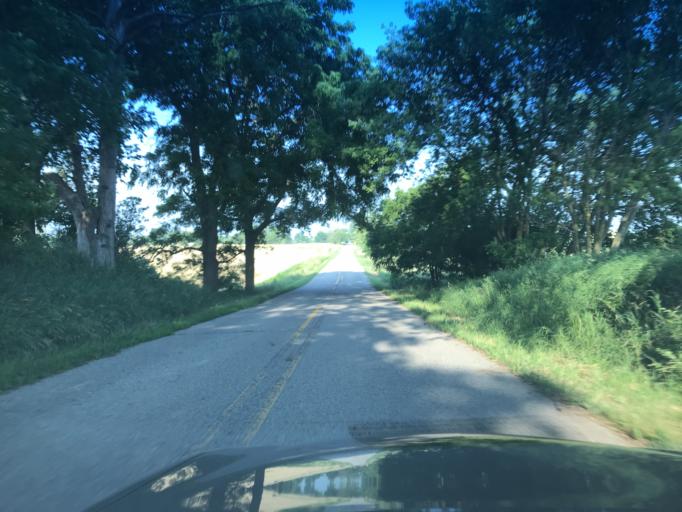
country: US
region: Michigan
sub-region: Ingham County
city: Mason
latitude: 42.5531
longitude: -84.4701
